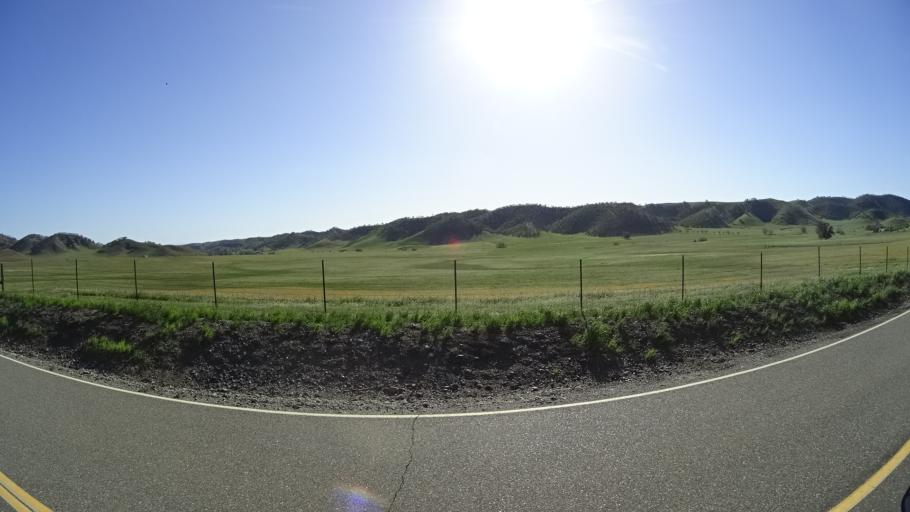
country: US
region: California
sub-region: Tehama County
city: Rancho Tehama Reserve
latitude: 39.7547
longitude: -122.5261
